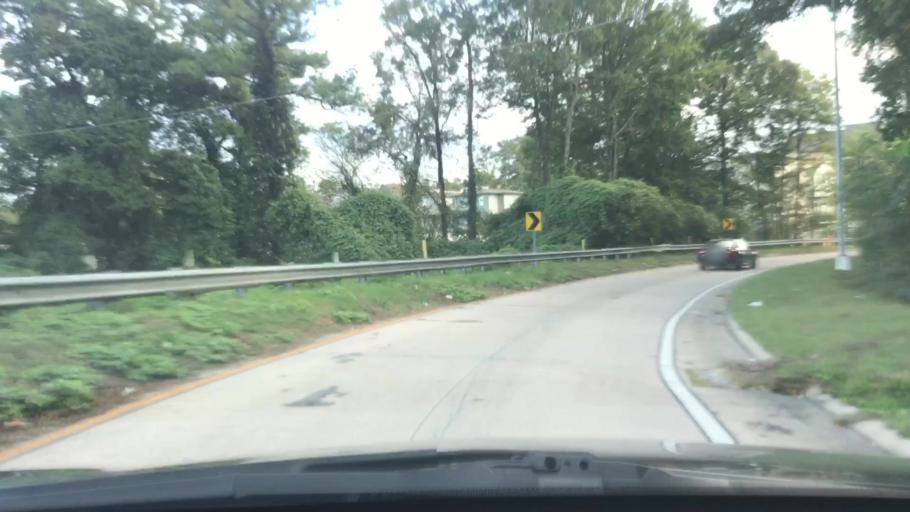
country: US
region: Georgia
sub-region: DeKalb County
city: Druid Hills
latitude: 33.8131
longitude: -84.3648
